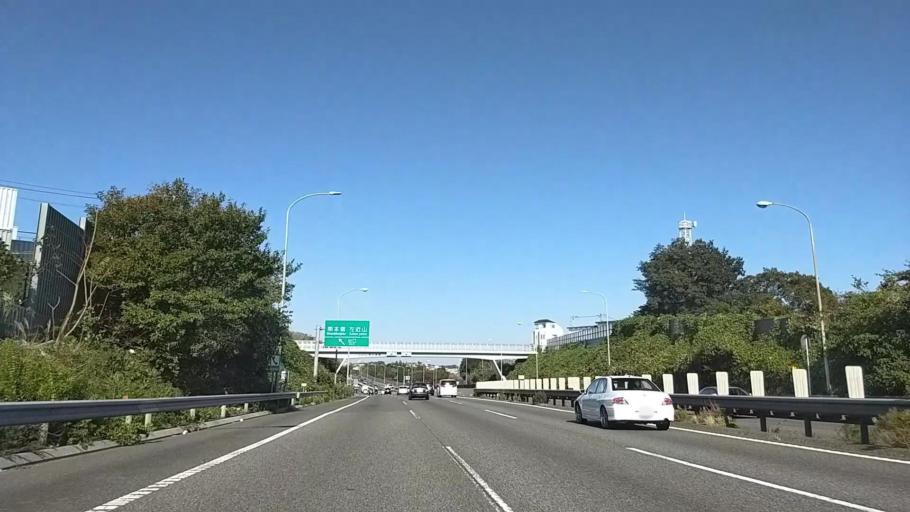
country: JP
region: Kanagawa
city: Yokohama
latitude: 35.4595
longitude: 139.5454
